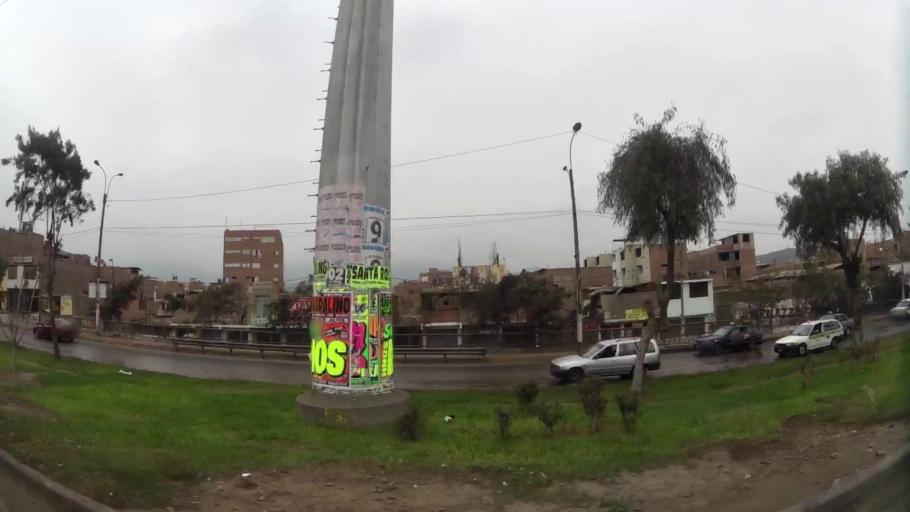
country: PE
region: Lima
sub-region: Lima
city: Independencia
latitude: -11.9845
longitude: -77.0787
